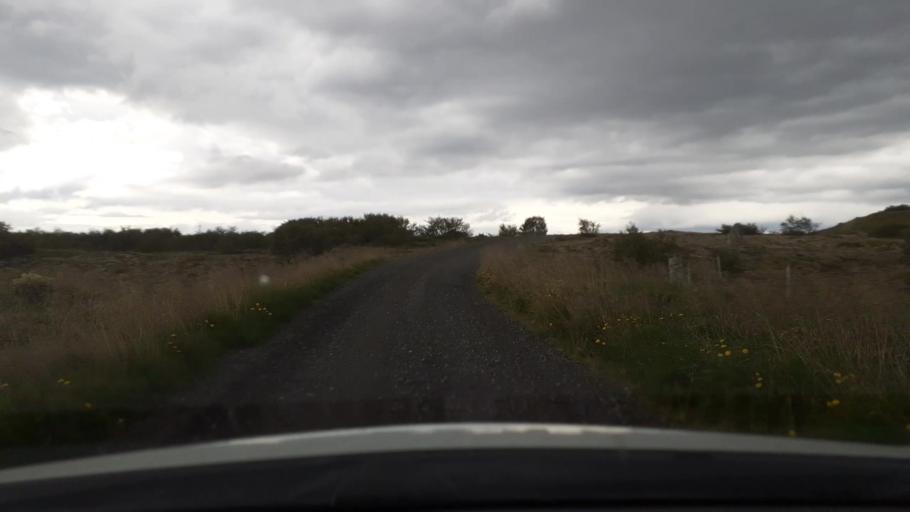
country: IS
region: West
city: Borgarnes
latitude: 64.6388
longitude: -21.7487
